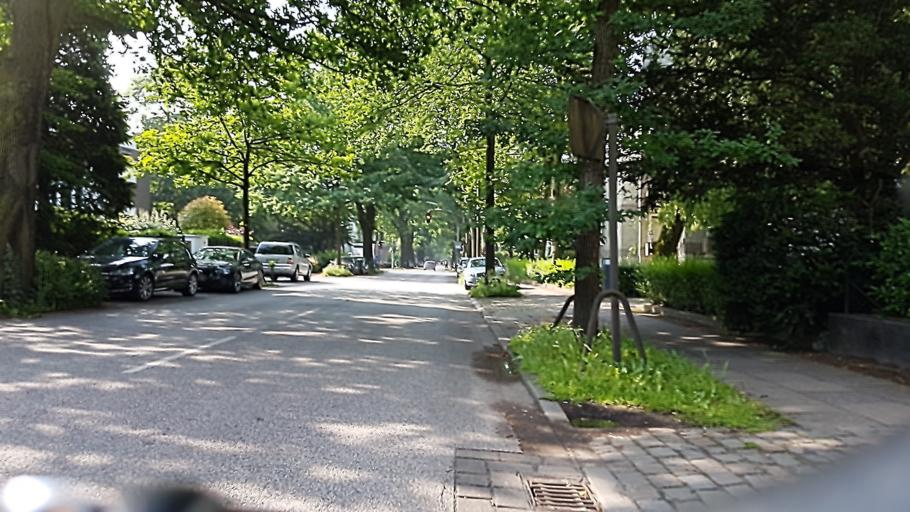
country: DE
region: Hamburg
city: Hamburg
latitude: 53.5751
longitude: 10.0116
